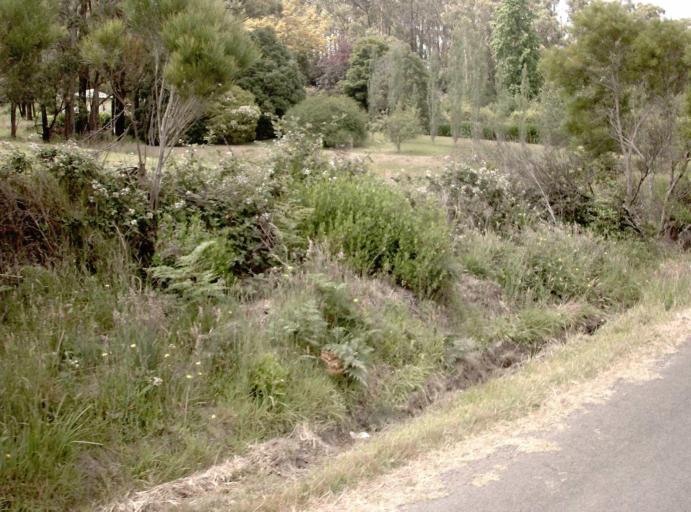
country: AU
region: Victoria
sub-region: Baw Baw
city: Warragul
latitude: -38.4287
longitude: 146.0372
